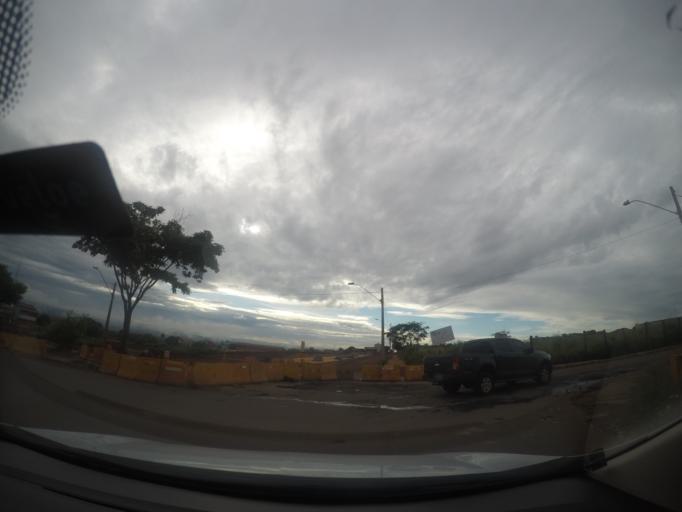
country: BR
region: Goias
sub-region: Goiania
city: Goiania
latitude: -16.6092
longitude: -49.3146
